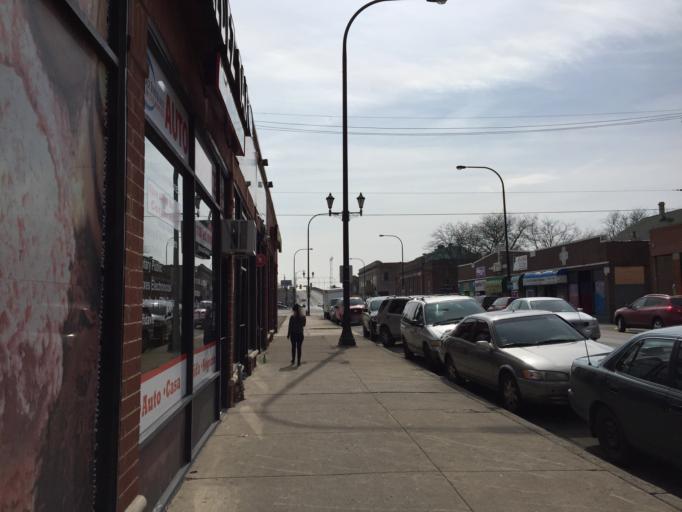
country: US
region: Illinois
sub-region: Cook County
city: Cicero
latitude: 41.8473
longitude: -87.7539
